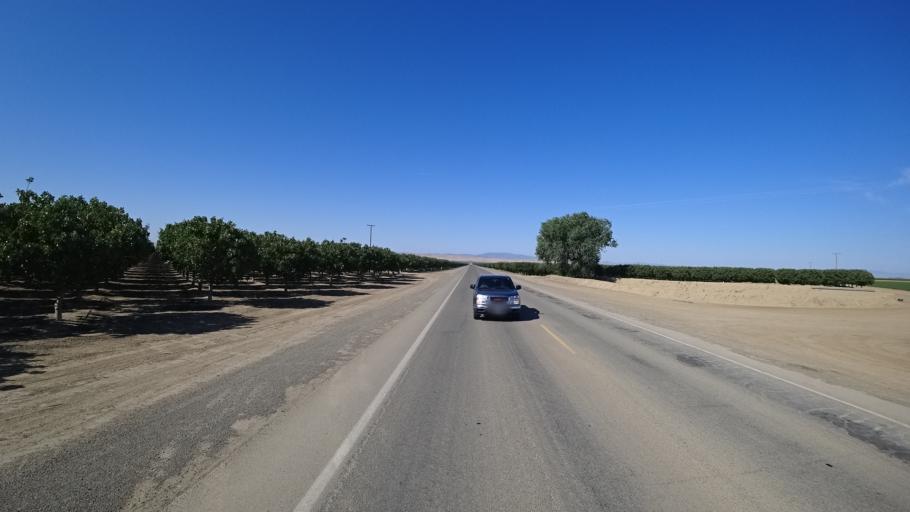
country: US
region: California
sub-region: Fresno County
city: Huron
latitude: 36.1230
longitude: -120.0302
